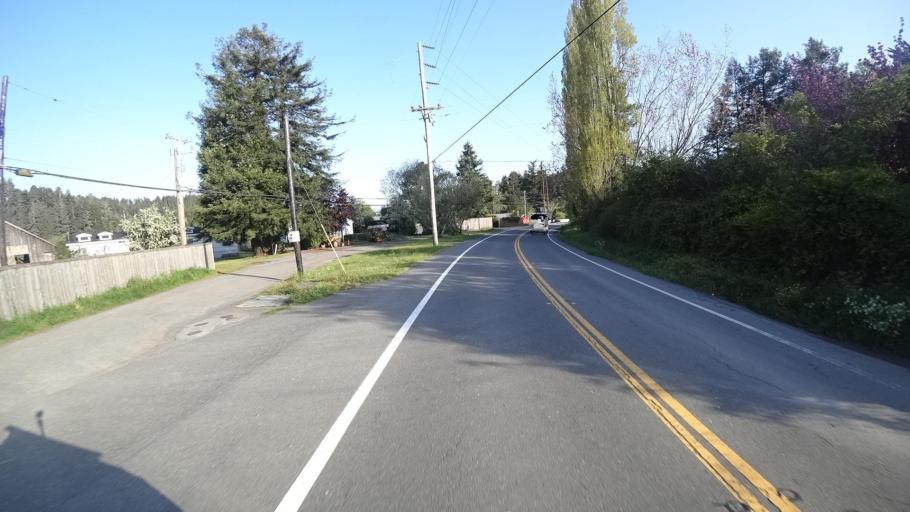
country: US
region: California
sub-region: Humboldt County
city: Myrtletown
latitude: 40.7709
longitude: -124.0733
